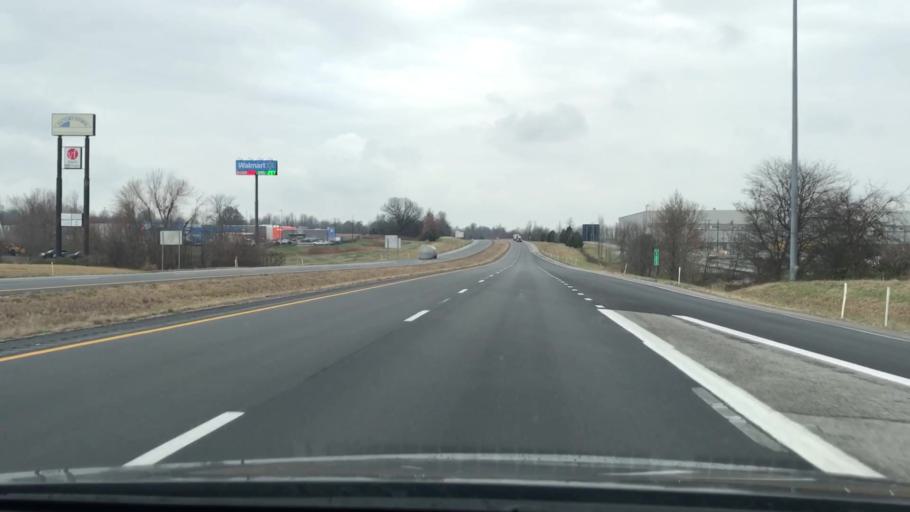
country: US
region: Kentucky
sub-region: Hopkins County
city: Madisonville
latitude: 37.4192
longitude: -87.4722
